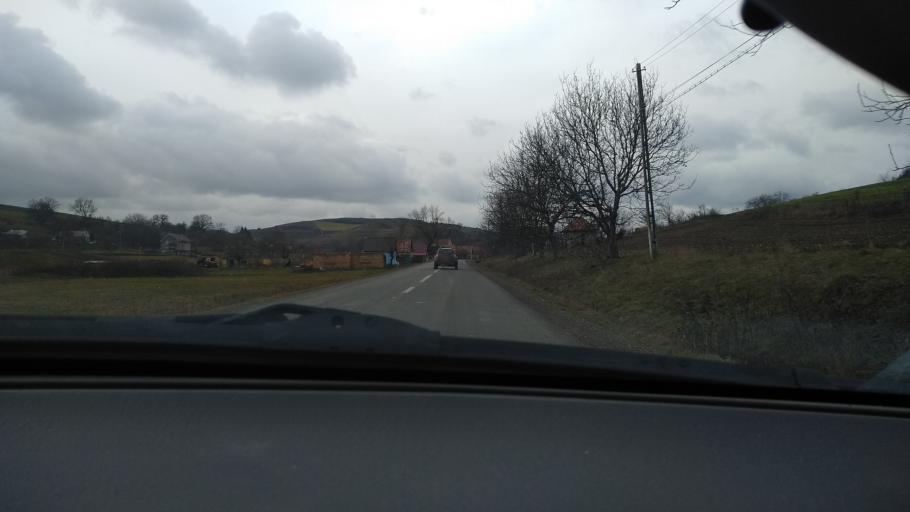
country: RO
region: Mures
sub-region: Comuna Galesti
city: Galesti
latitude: 46.5436
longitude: 24.7417
